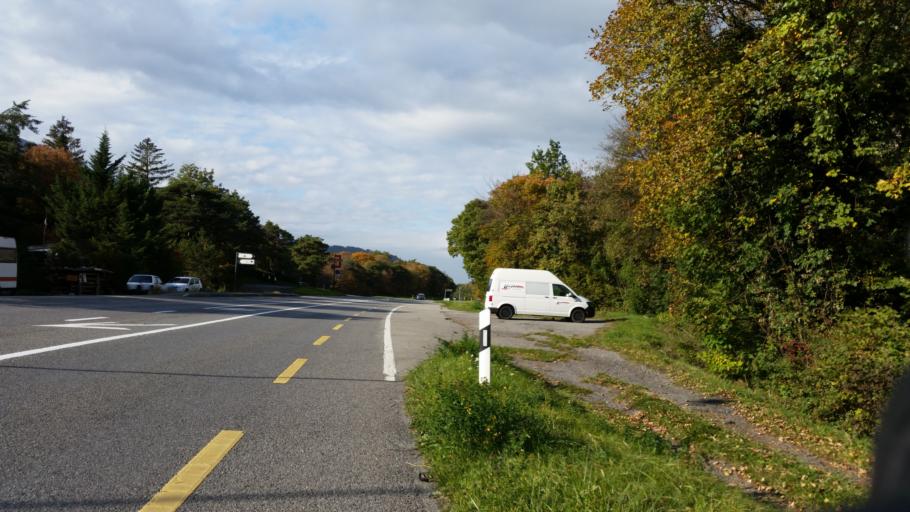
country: CH
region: Valais
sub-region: Martigny District
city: Evionnaz
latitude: 46.1899
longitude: 7.0260
